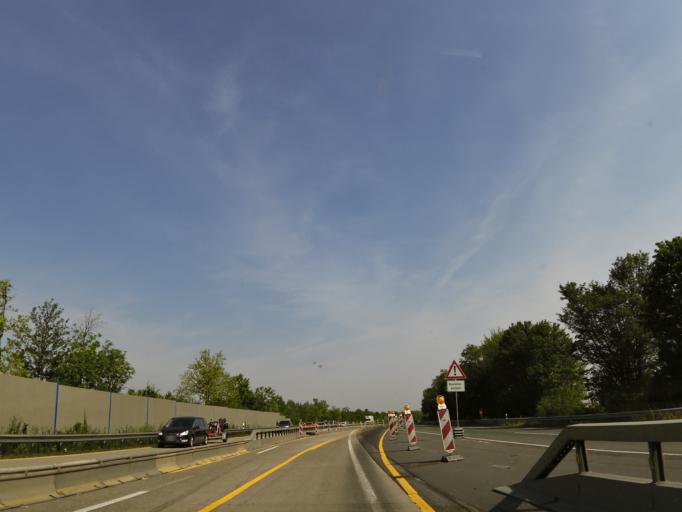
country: DE
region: Rheinland-Pfalz
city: Dintesheim
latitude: 49.7177
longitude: 8.1356
